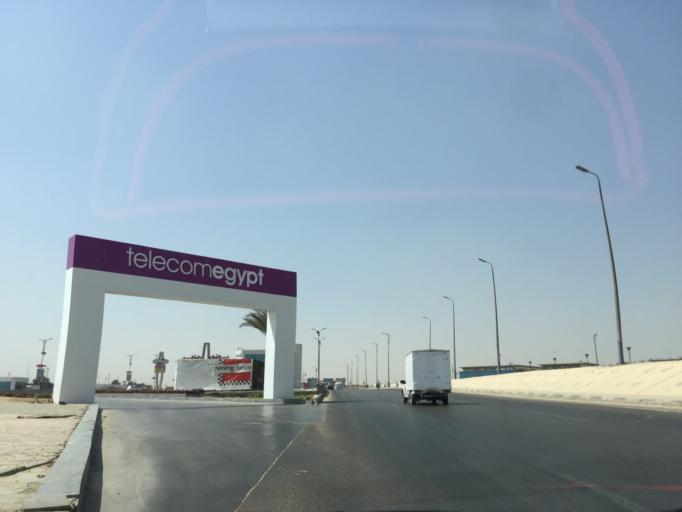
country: EG
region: Al Jizah
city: Awsim
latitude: 30.0657
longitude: 31.0216
